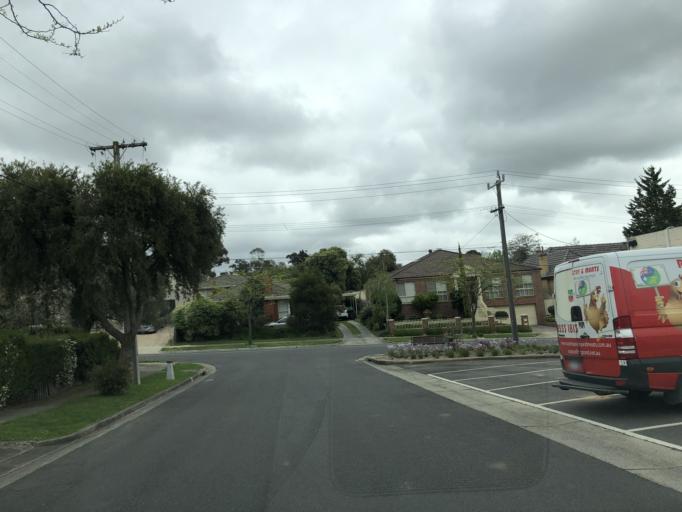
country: AU
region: Victoria
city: Burwood East
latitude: -37.8554
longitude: 145.1438
